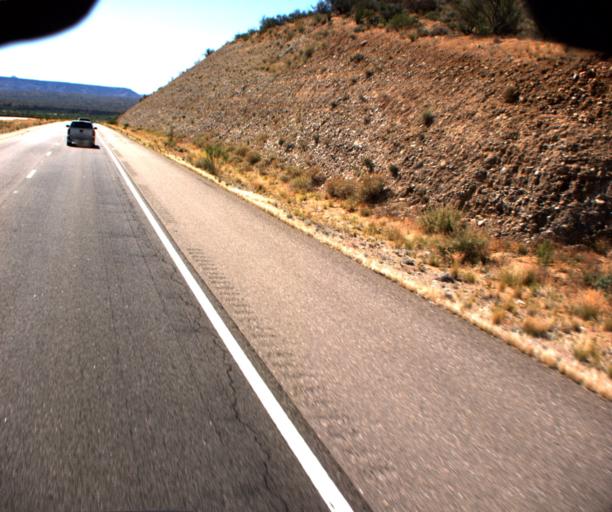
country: US
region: Arizona
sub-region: Yavapai County
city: Bagdad
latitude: 34.3872
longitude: -113.2040
